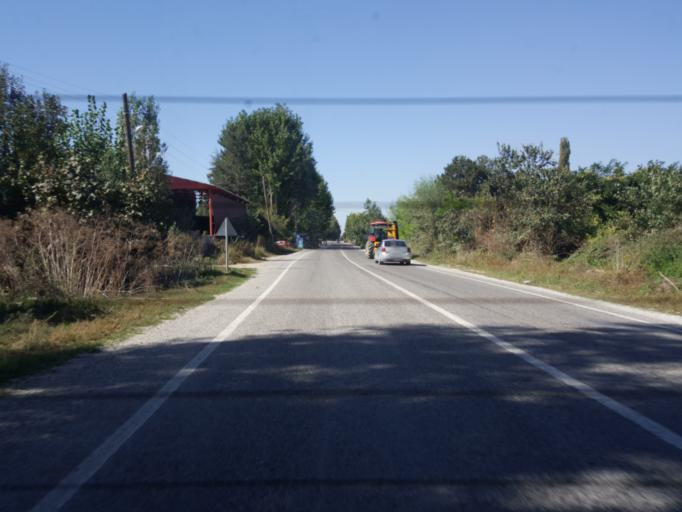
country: TR
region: Tokat
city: Pazar
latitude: 40.2703
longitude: 36.2457
